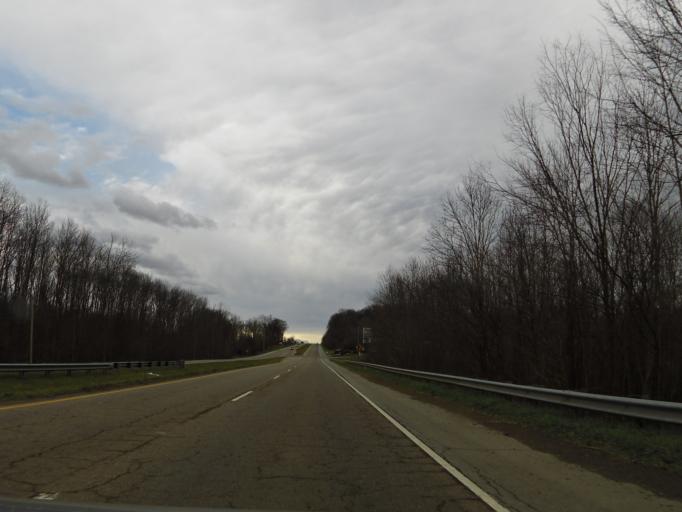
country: US
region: Tennessee
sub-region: Washington County
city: Jonesborough
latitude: 36.2437
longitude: -82.6146
